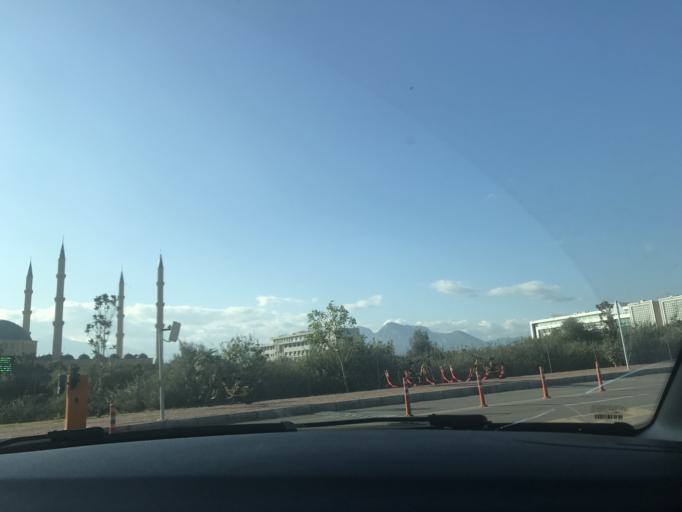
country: TR
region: Antalya
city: Antalya
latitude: 36.8893
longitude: 30.6462
